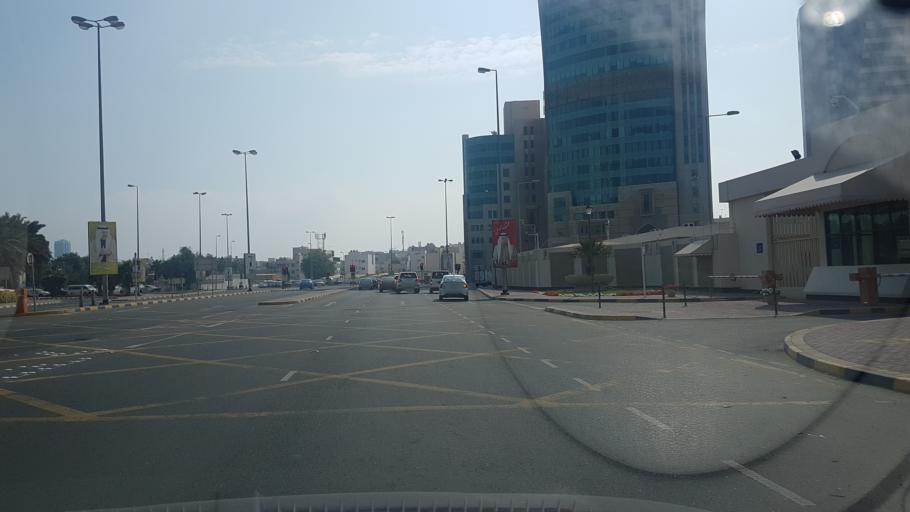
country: BH
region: Manama
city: Manama
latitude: 26.2384
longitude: 50.5805
